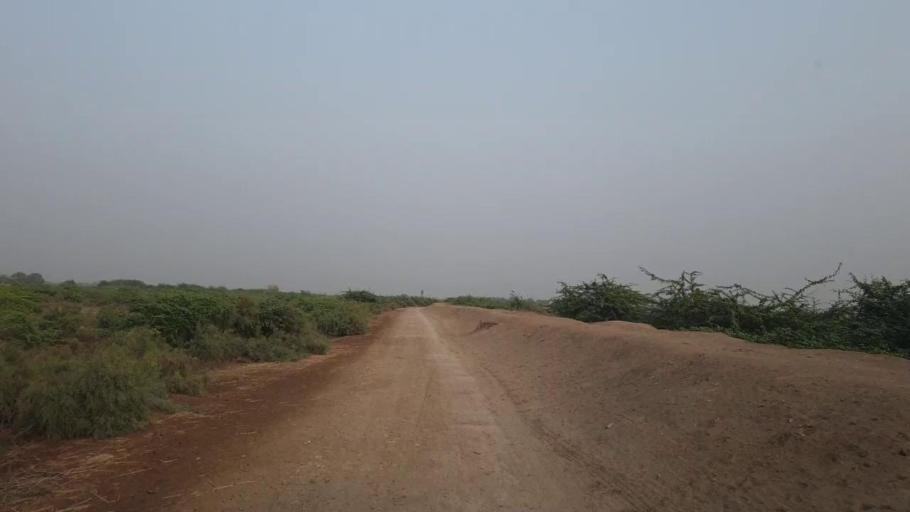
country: PK
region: Sindh
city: Mirpur Batoro
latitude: 24.6422
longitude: 68.3787
